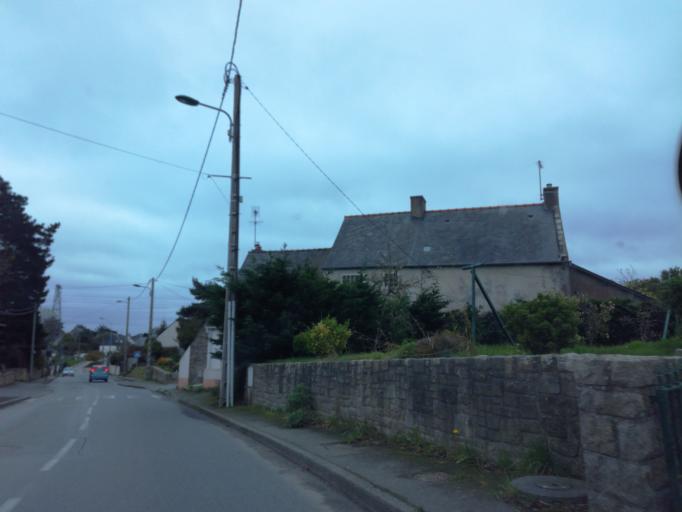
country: FR
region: Brittany
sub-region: Departement d'Ille-et-Vilaine
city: La Richardais
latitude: 48.6100
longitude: -2.0438
